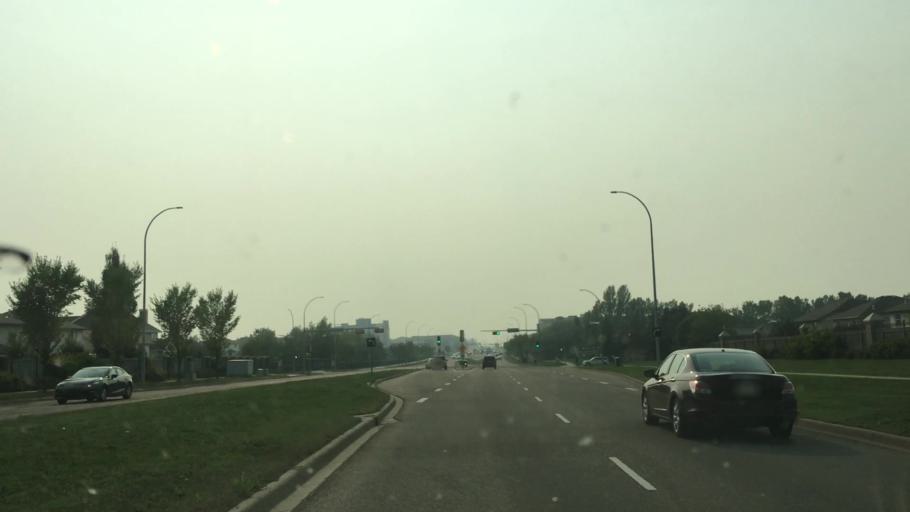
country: CA
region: Alberta
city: Beaumont
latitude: 53.4249
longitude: -113.5070
